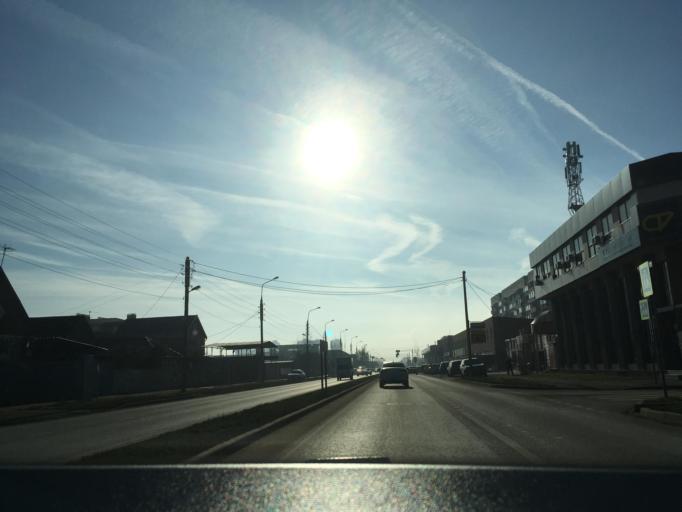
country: RU
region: Krasnodarskiy
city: Krasnodar
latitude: 45.1167
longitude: 39.0117
